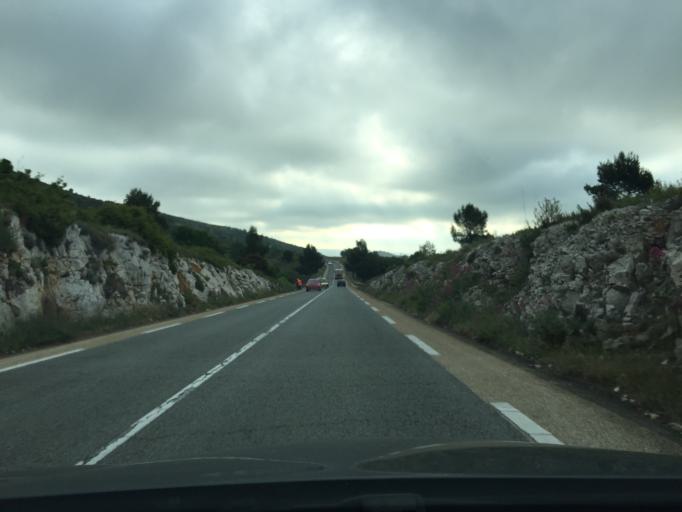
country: FR
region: Provence-Alpes-Cote d'Azur
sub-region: Departement des Bouches-du-Rhone
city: La Penne-sur-Huveaune
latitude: 43.2389
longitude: 5.4778
